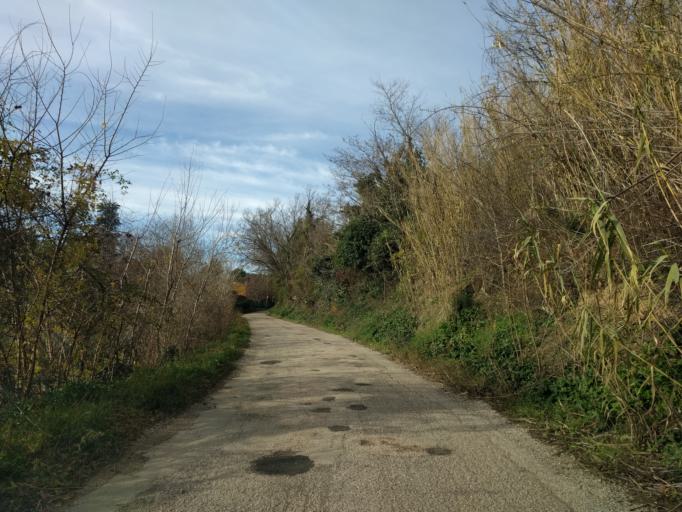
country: IT
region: The Marches
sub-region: Provincia di Pesaro e Urbino
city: Cuccurano
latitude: 43.8078
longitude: 12.9531
